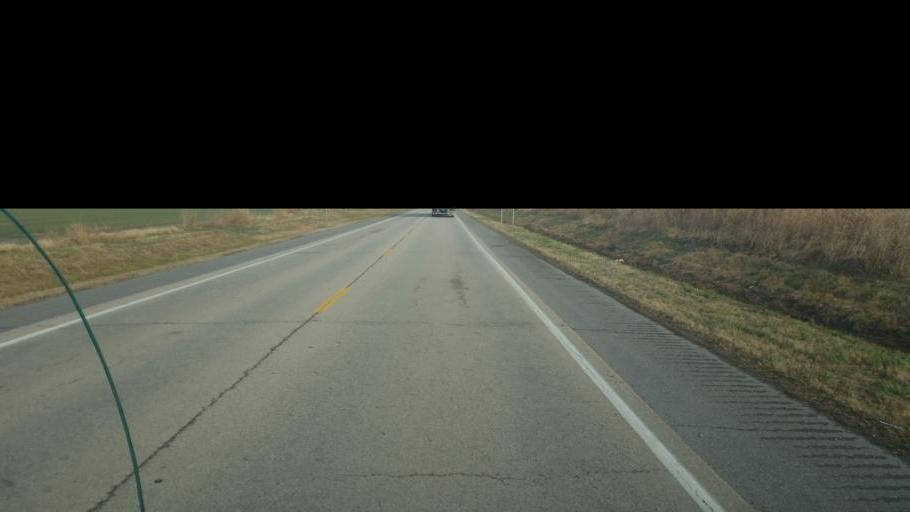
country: US
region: Missouri
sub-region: Stoddard County
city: Bloomfield
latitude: 36.9024
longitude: -89.9226
